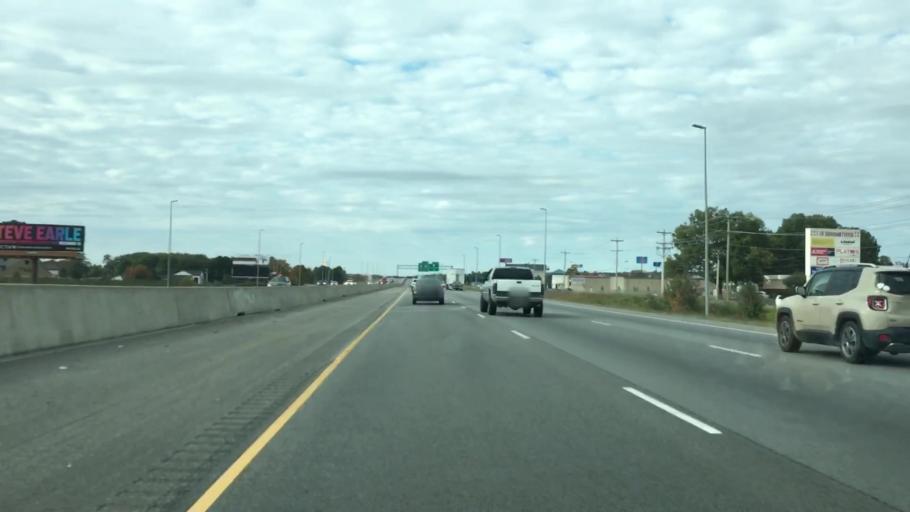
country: US
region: Arkansas
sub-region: Faulkner County
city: Conway
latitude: 35.0854
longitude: -92.4162
